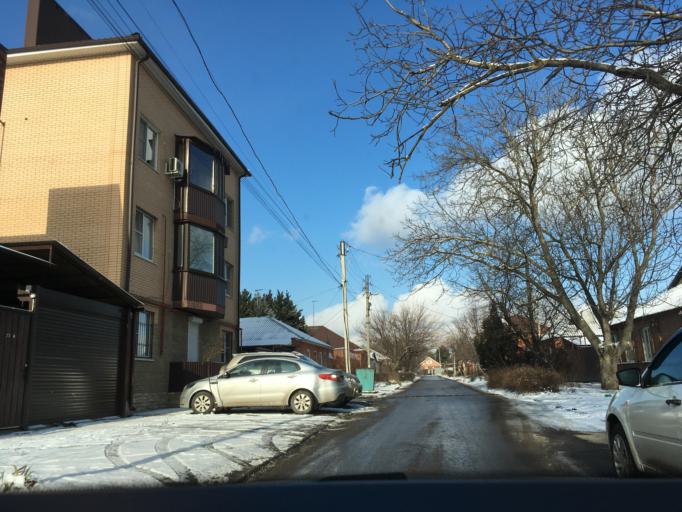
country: RU
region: Rostov
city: Rostov-na-Donu
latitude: 47.2343
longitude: 39.6294
